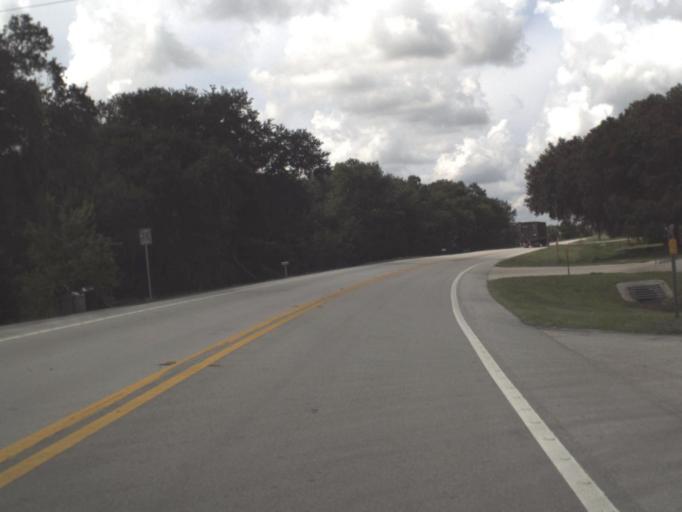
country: US
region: Florida
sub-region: Glades County
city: Buckhead Ridge
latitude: 27.2364
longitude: -80.9887
